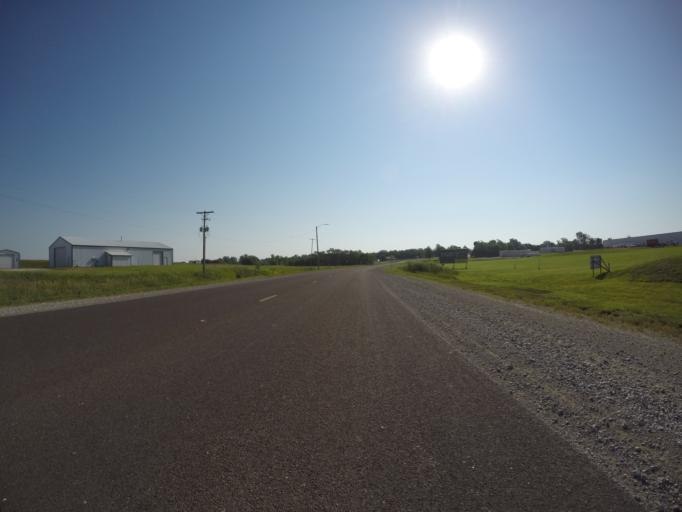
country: US
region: Kansas
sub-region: Brown County
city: Hiawatha
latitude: 39.8521
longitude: -95.5535
